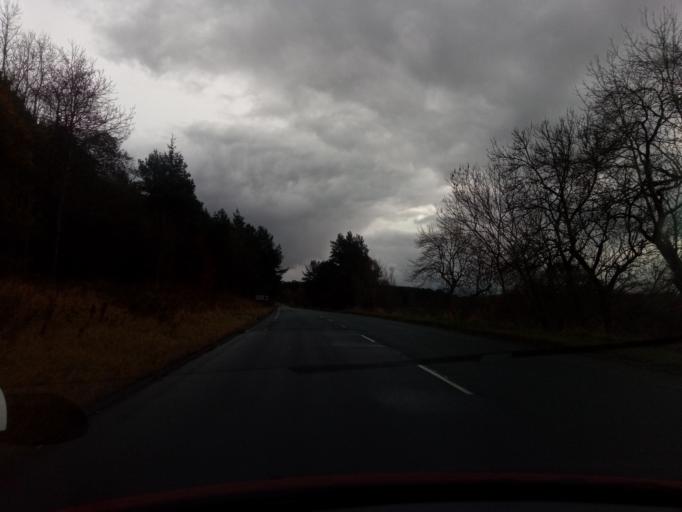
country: GB
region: England
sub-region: Northumberland
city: Rochester
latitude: 55.2798
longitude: -2.2780
